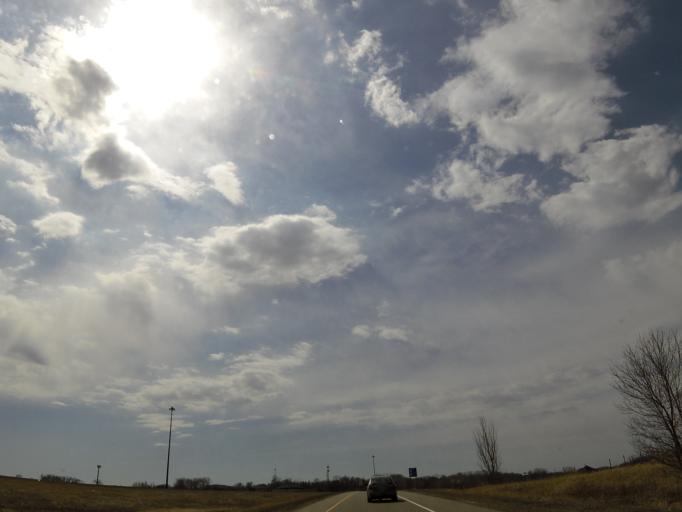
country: US
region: Minnesota
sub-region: Dakota County
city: Eagan
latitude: 44.8153
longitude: -93.2239
